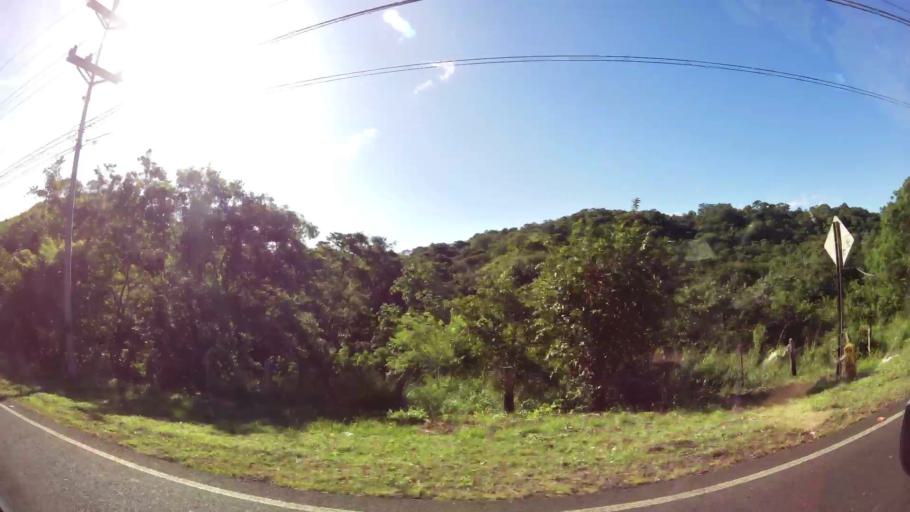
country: CR
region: Guanacaste
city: Belen
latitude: 10.3689
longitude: -85.6412
